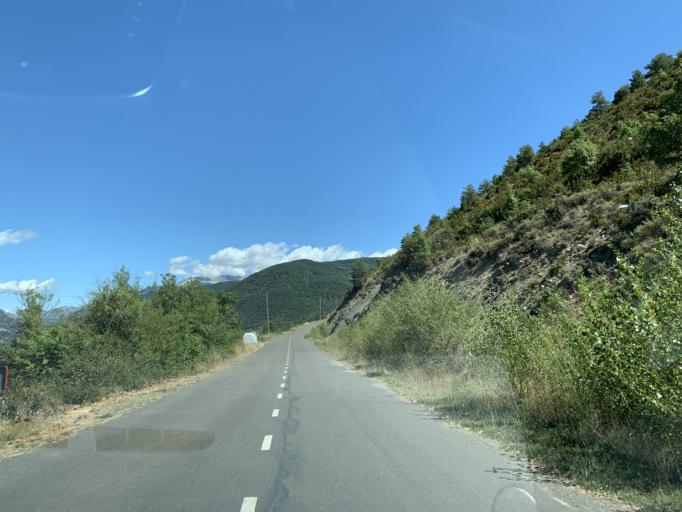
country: ES
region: Aragon
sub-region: Provincia de Huesca
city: Sabinanigo
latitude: 42.5558
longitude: -0.3177
